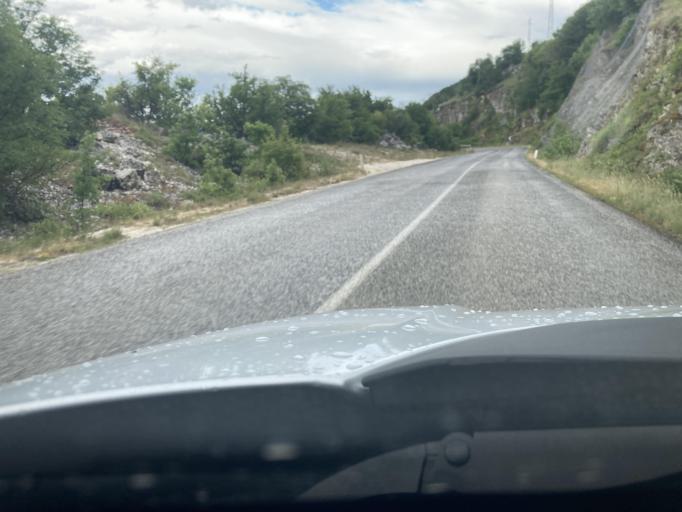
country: IT
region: Abruzzo
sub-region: Provincia dell' Aquila
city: San Panfilo d'Ocre
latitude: 42.2752
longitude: 13.4800
